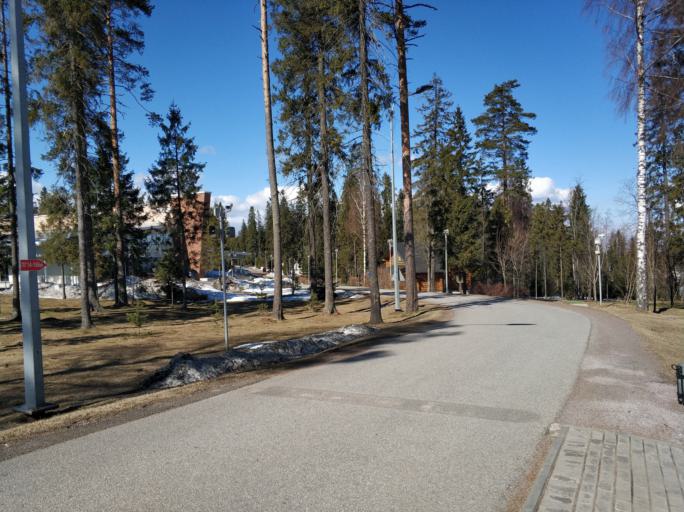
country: RU
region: Leningrad
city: Sosnovo
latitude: 60.5161
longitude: 30.2103
